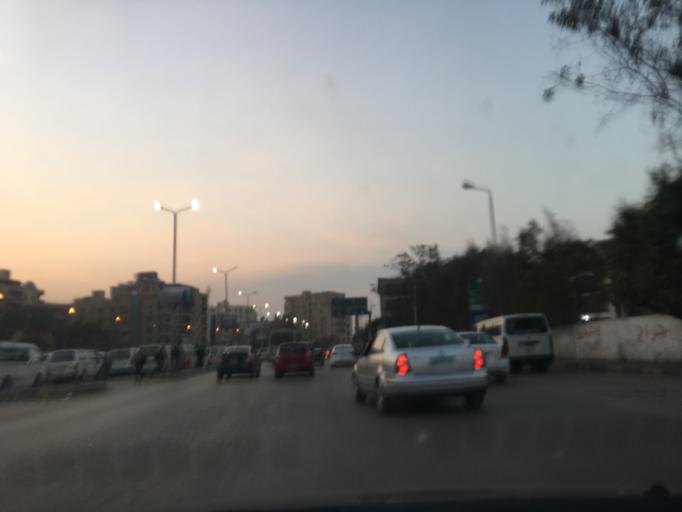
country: EG
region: Al Jizah
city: Al Jizah
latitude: 29.9906
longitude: 31.1329
